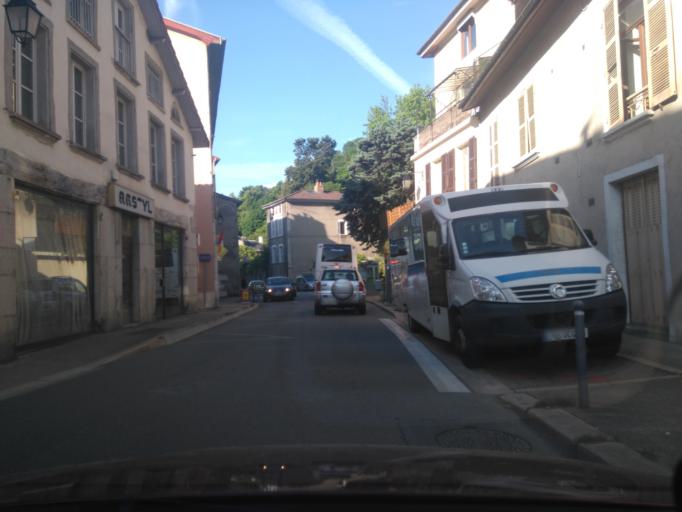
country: FR
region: Rhone-Alpes
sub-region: Departement de l'Isere
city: La Tronche
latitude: 45.2022
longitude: 5.7346
